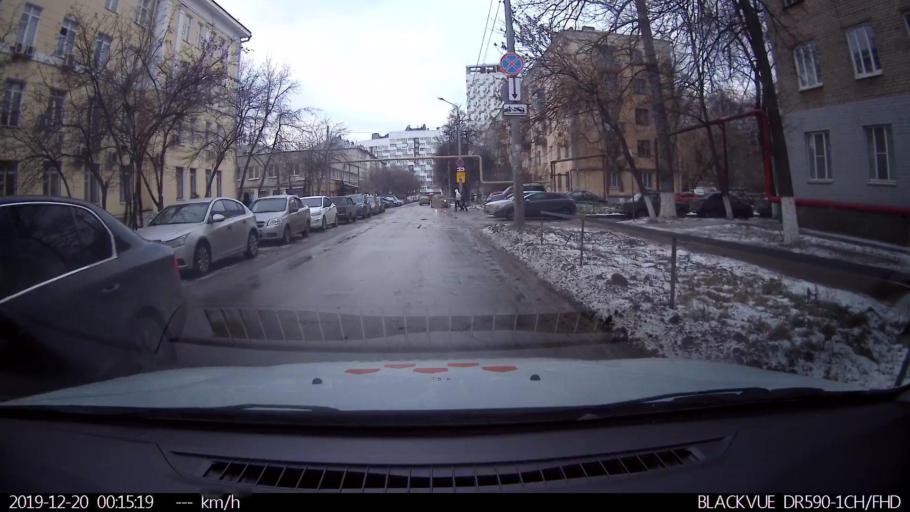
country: RU
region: Jaroslavl
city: Porech'ye-Rybnoye
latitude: 56.9941
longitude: 39.3873
